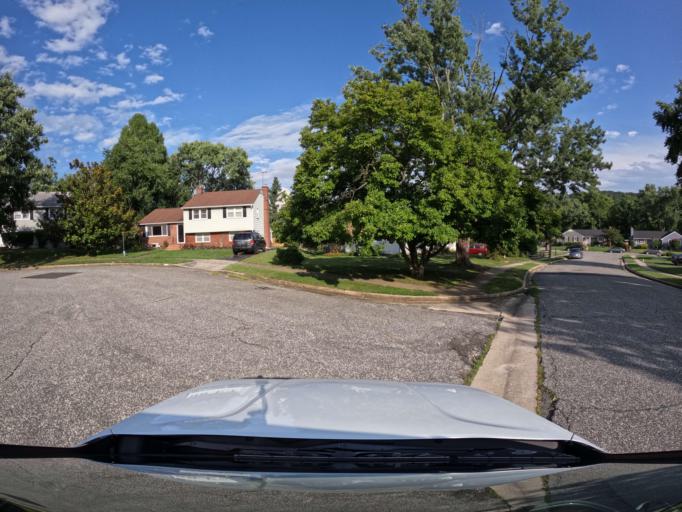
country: US
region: Maryland
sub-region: Baltimore County
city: Mays Chapel
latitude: 39.4177
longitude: -76.6438
